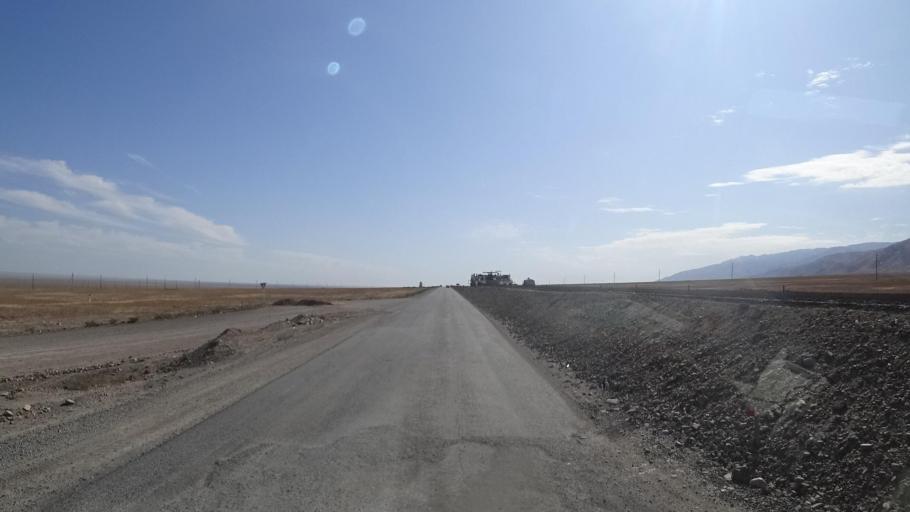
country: KG
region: Chuy
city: Ivanovka
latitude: 43.3845
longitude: 75.1729
